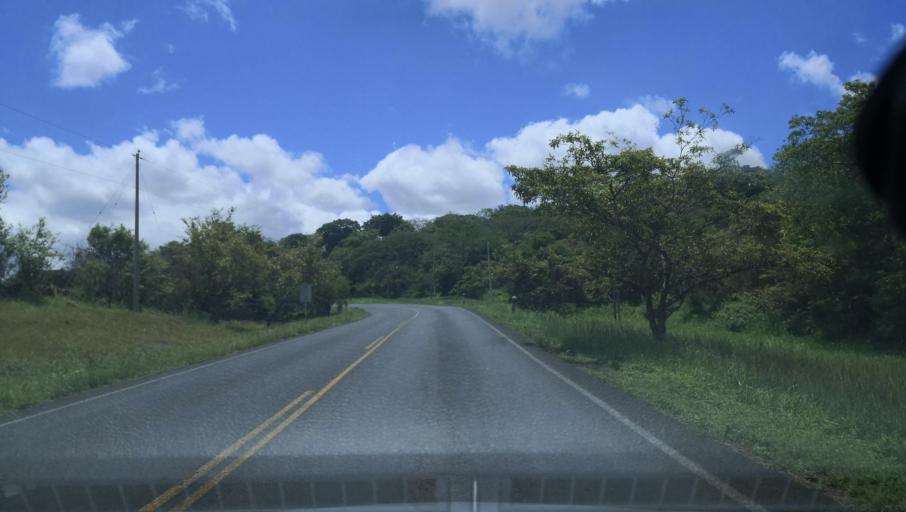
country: NI
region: Esteli
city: Esteli
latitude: 13.2100
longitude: -86.3774
